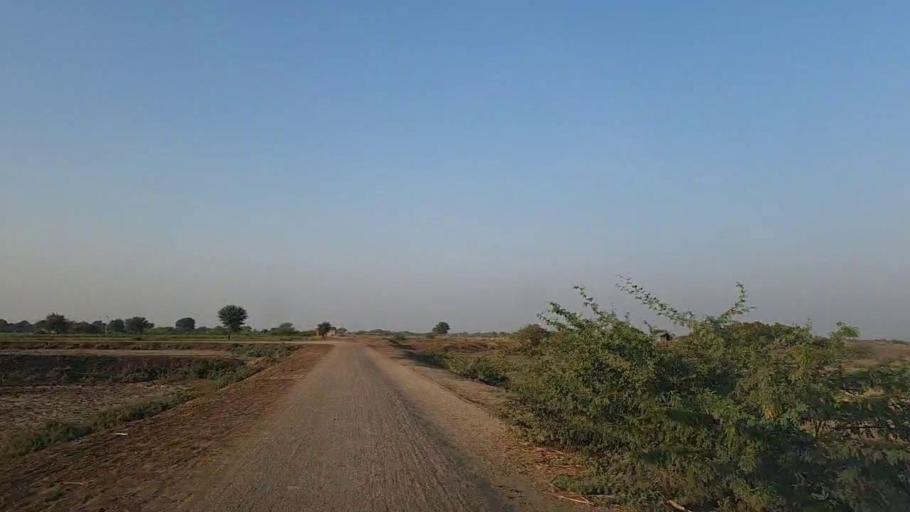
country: PK
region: Sindh
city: Naukot
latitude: 24.9577
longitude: 69.4521
